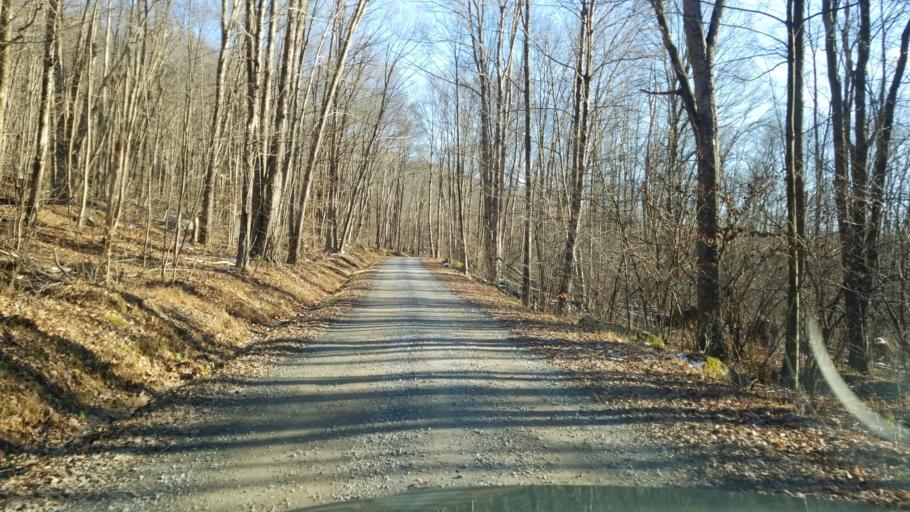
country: US
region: Pennsylvania
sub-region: Jefferson County
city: Brockway
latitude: 41.2865
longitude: -78.8278
